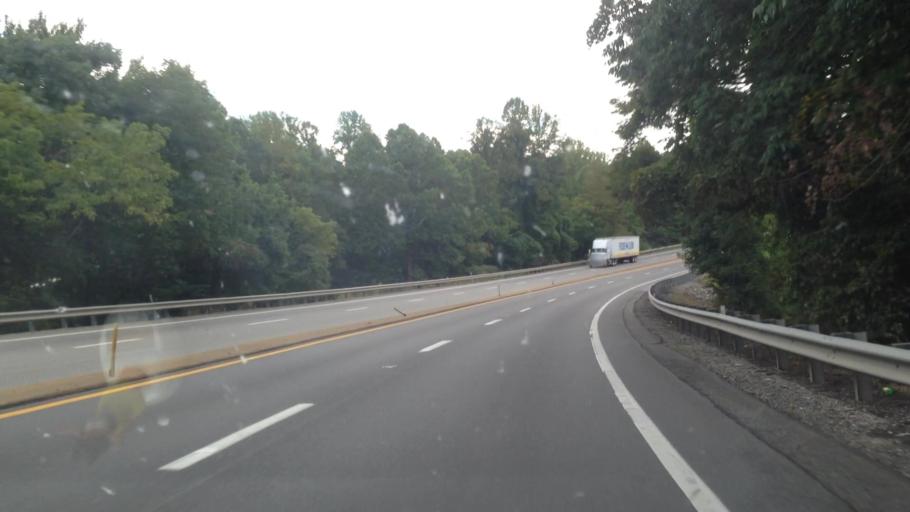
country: US
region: Virginia
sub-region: Henry County
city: Chatmoss
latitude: 36.5823
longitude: -79.8622
